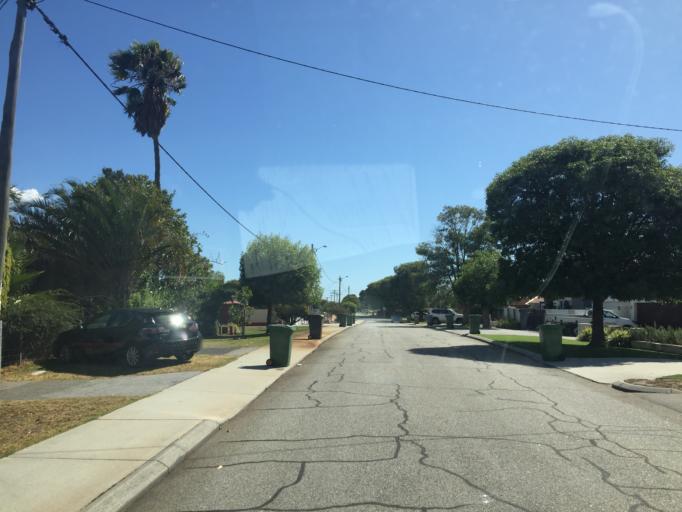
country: AU
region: Western Australia
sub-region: Belmont
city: Redcliffe
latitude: -31.9349
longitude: 115.9390
